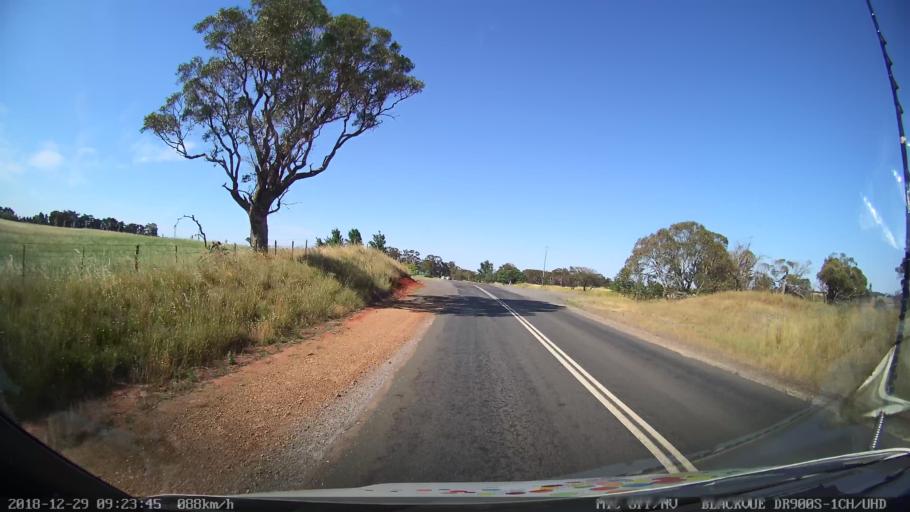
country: AU
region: New South Wales
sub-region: Upper Lachlan Shire
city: Crookwell
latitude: -34.5282
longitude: 149.3973
